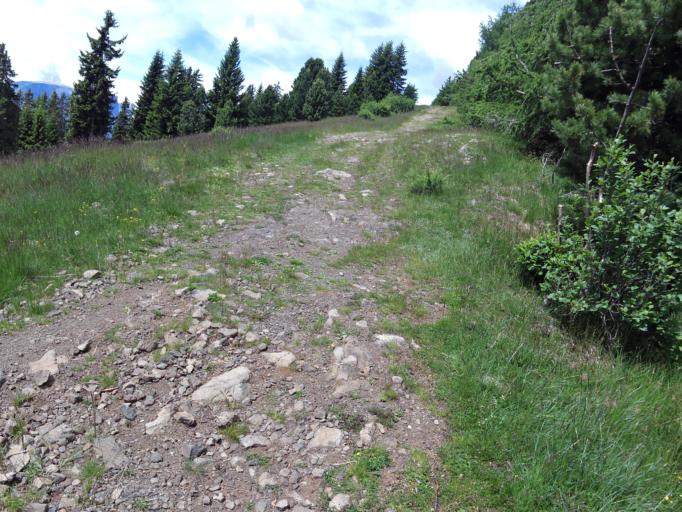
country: IT
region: Trentino-Alto Adige
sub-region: Bolzano
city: Ortisei
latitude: 46.5582
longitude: 11.6632
